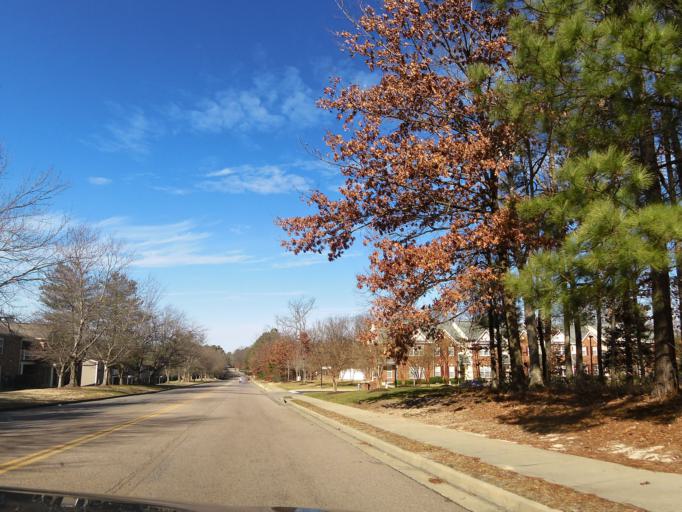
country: US
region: Virginia
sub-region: Henrico County
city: Tuckahoe
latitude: 37.6290
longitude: -77.5539
